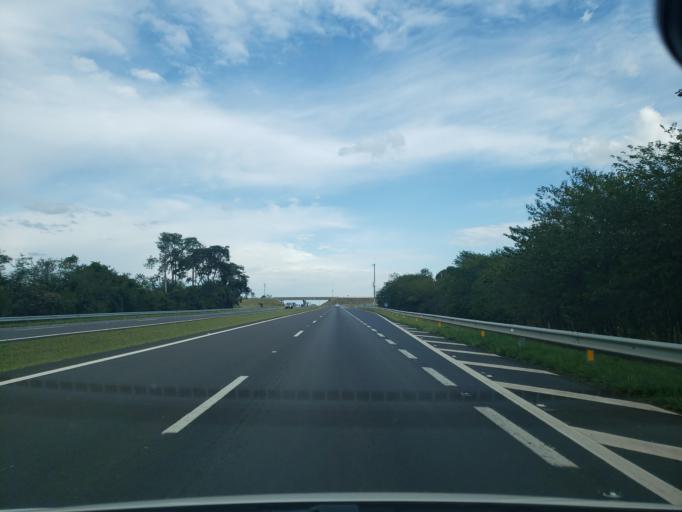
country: BR
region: Sao Paulo
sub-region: Itirapina
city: Itirapina
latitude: -22.2675
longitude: -47.9306
